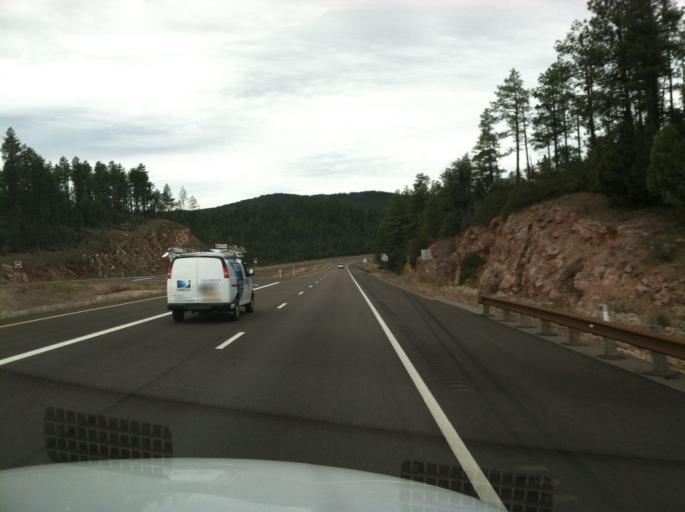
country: US
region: Arizona
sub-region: Gila County
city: Star Valley
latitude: 34.3238
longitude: -111.0738
